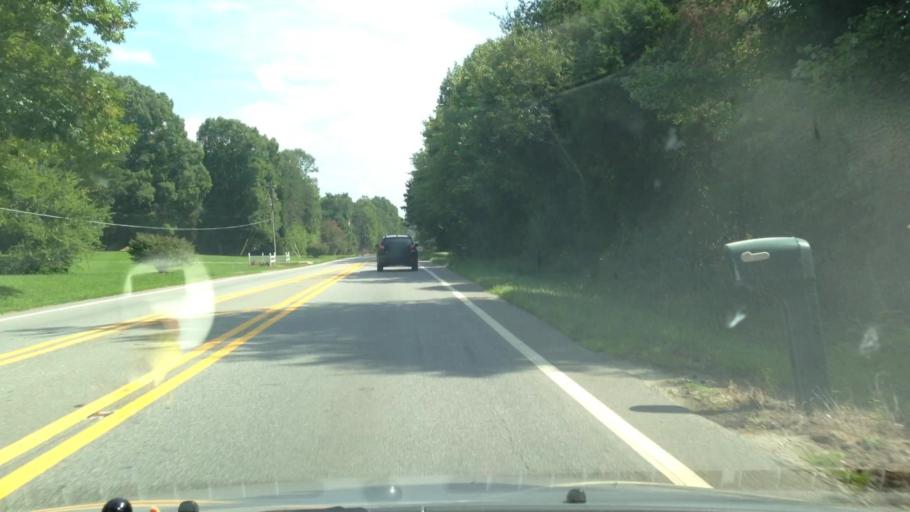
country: US
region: North Carolina
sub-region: Guilford County
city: Stokesdale
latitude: 36.2098
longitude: -79.9888
